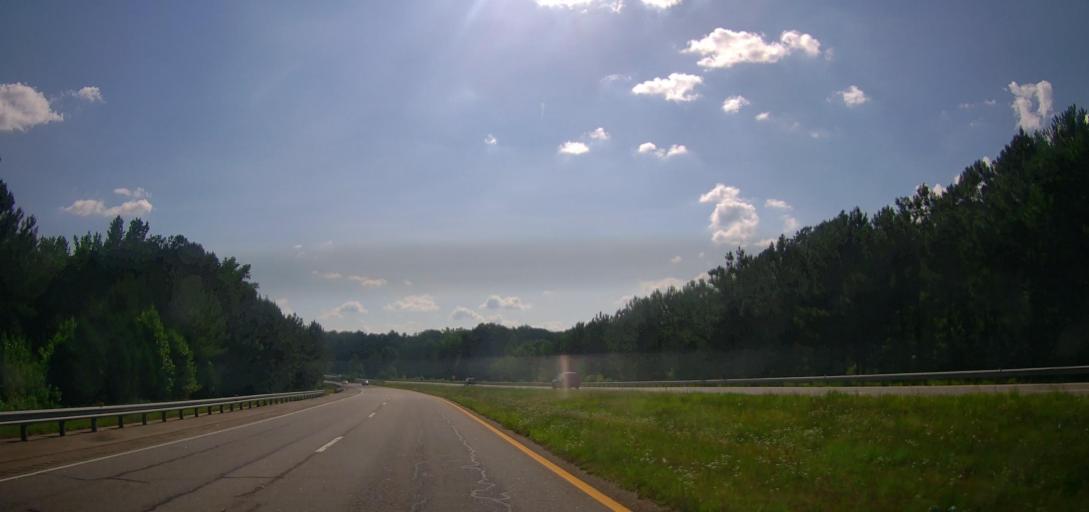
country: US
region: Georgia
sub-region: Henry County
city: Hampton
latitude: 33.3955
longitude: -84.2492
